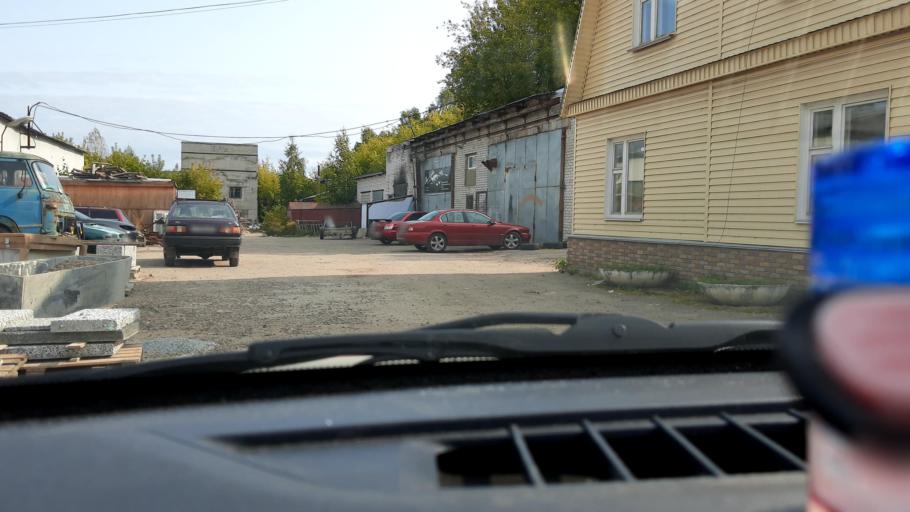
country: RU
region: Nizjnij Novgorod
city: Nizhniy Novgorod
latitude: 56.2436
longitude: 43.9945
